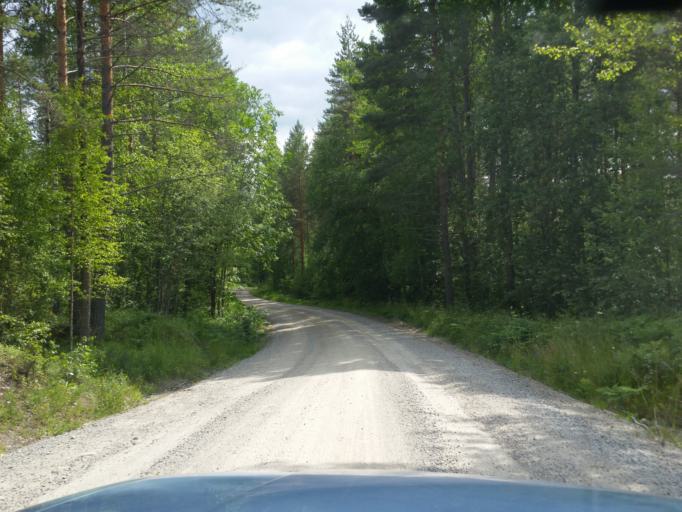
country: FI
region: Southern Savonia
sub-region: Savonlinna
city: Sulkava
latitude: 61.7244
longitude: 28.3167
